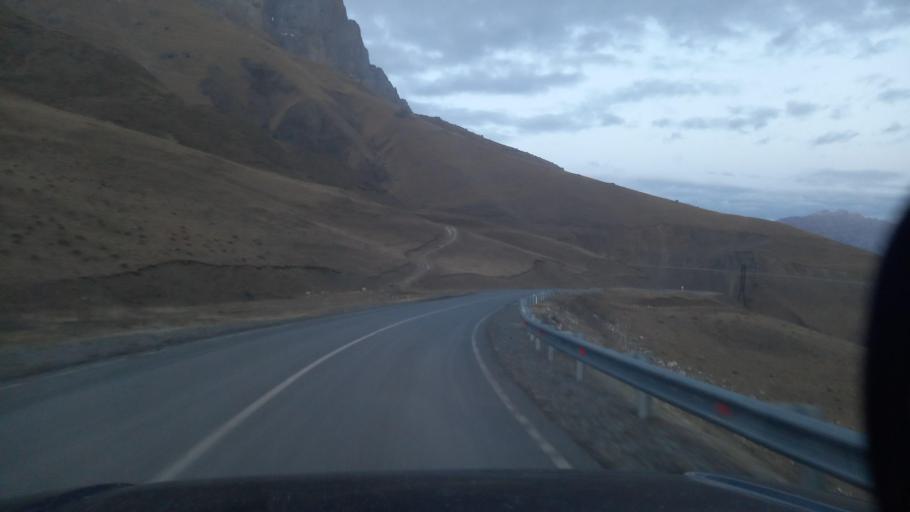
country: RU
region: Ingushetiya
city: Dzhayrakh
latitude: 42.8188
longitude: 44.8408
